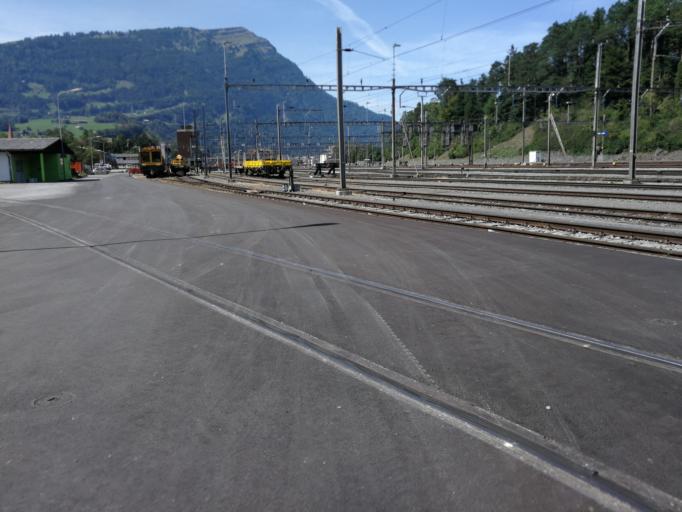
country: CH
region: Schwyz
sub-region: Bezirk Schwyz
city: Goldau
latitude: 47.0482
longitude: 8.5568
